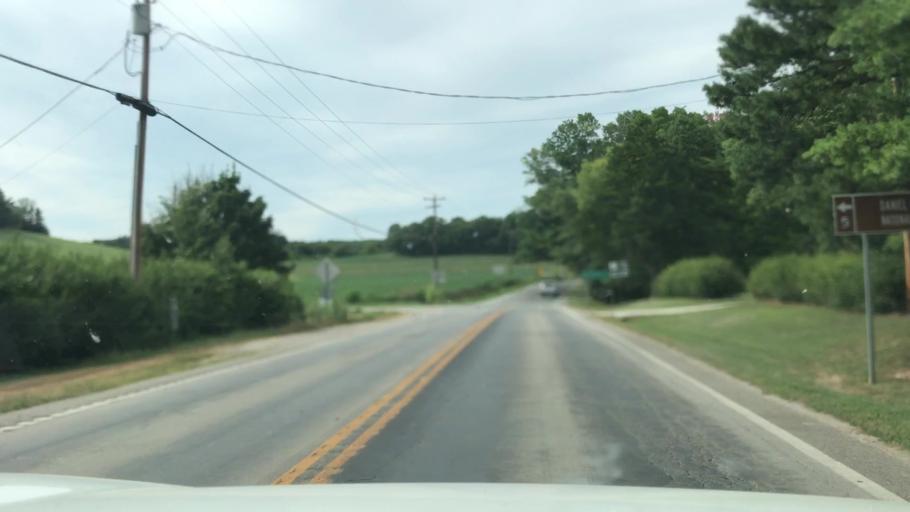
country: US
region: Missouri
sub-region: Saint Charles County
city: Weldon Spring
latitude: 38.6497
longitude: -90.7756
